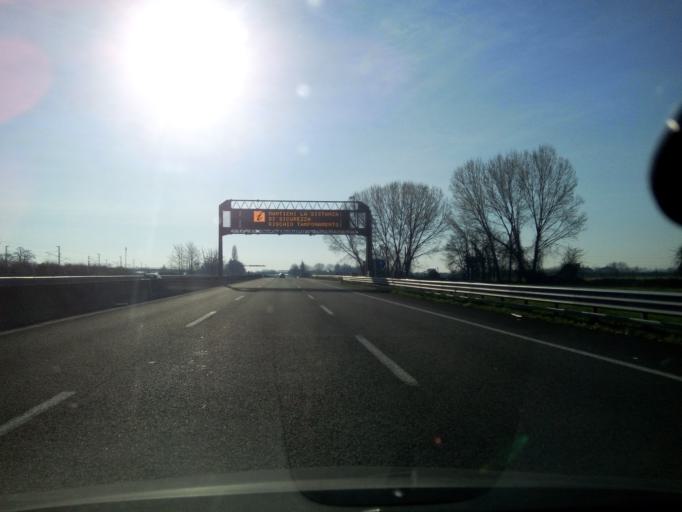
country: IT
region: Emilia-Romagna
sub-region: Provincia di Modena
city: Campogalliano
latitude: 44.6761
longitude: 10.8197
